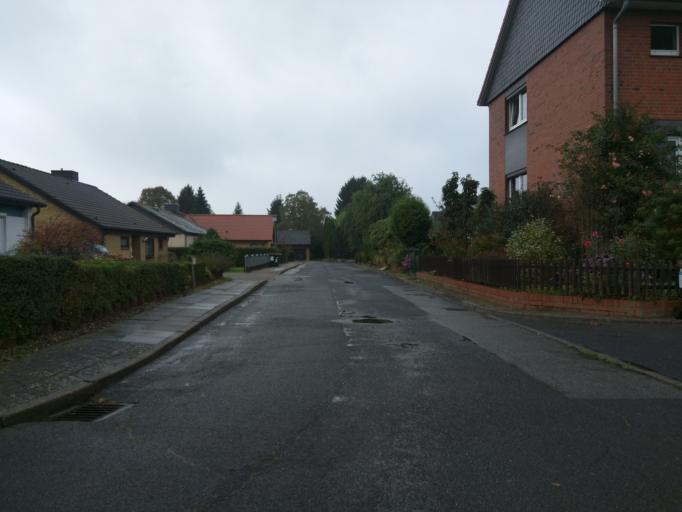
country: DE
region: Schleswig-Holstein
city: Lauenburg
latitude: 53.3732
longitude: 10.5451
